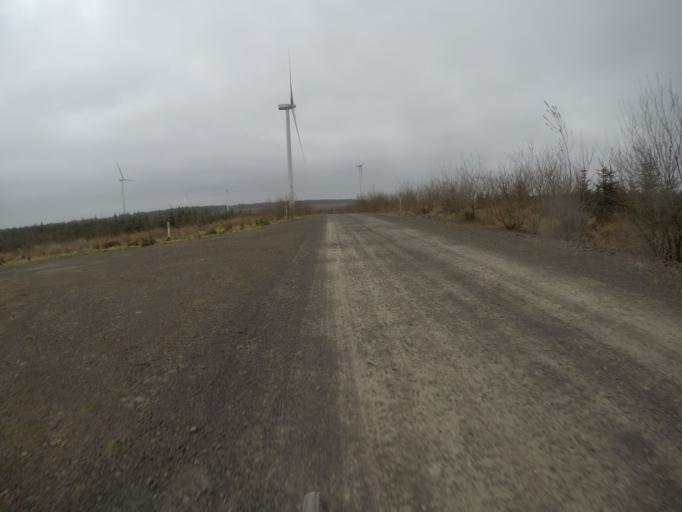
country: GB
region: Scotland
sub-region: East Ayrshire
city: Newmilns
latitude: 55.6507
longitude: -4.3255
